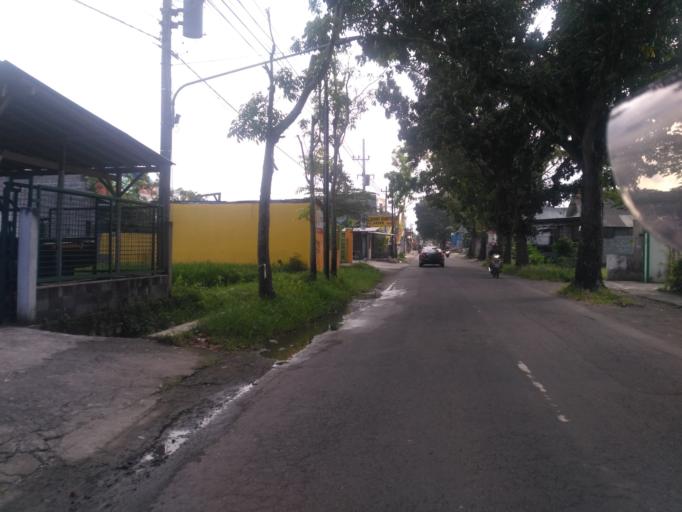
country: ID
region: Daerah Istimewa Yogyakarta
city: Yogyakarta
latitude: -7.7596
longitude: 110.3459
